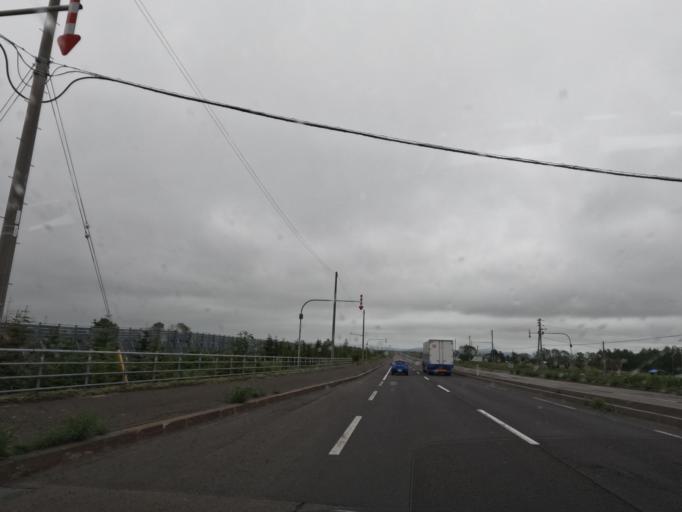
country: JP
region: Hokkaido
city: Tobetsu
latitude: 43.1645
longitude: 141.5201
